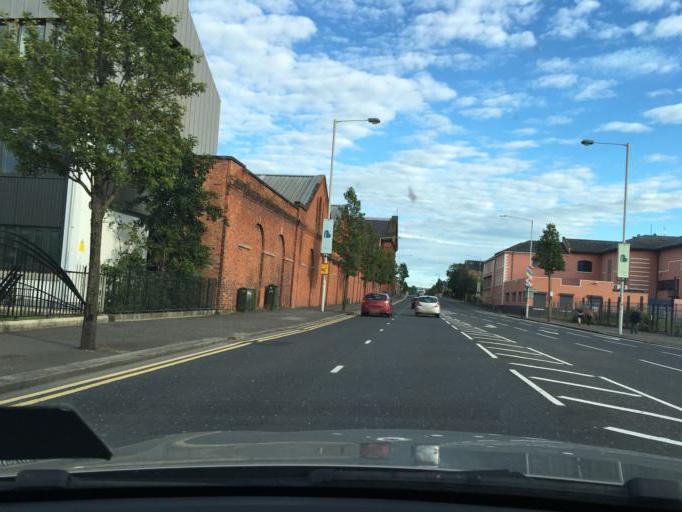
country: GB
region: Northern Ireland
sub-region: City of Belfast
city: Belfast
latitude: 54.5903
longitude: -5.9252
